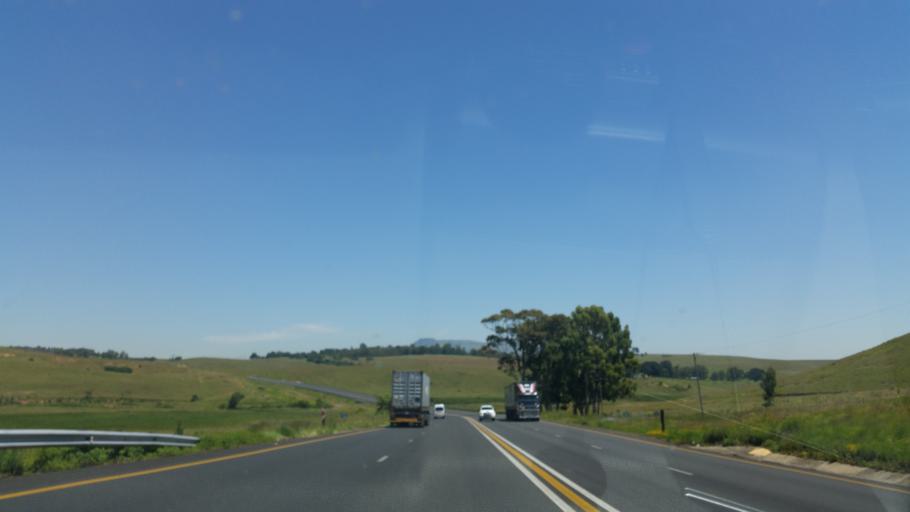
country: ZA
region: Orange Free State
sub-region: Thabo Mofutsanyana District Municipality
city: Harrismith
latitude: -28.3703
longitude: 29.3161
